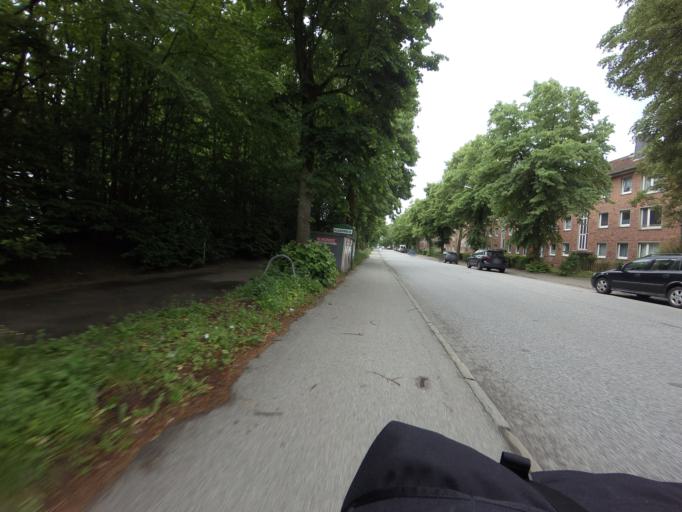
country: DE
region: Mecklenburg-Vorpommern
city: Selmsdorf
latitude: 53.9071
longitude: 10.8036
